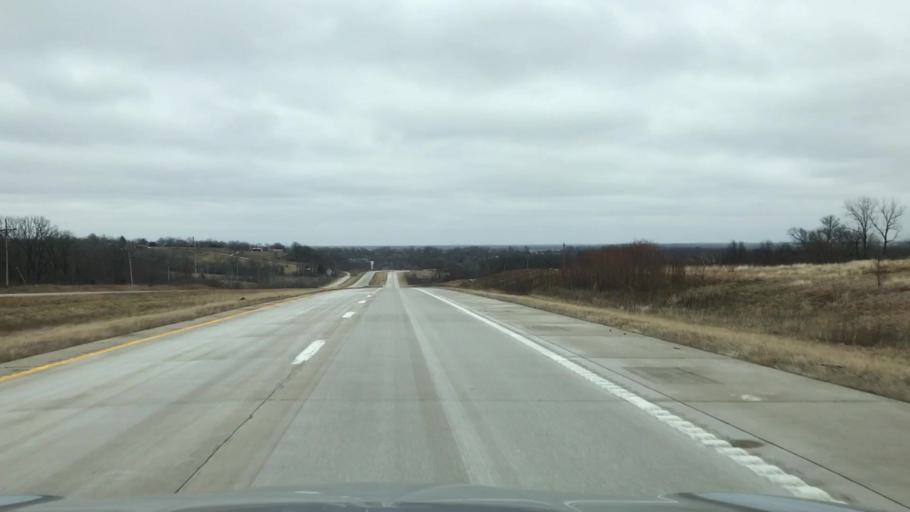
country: US
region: Missouri
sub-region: Livingston County
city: Chillicothe
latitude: 39.7395
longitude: -93.6564
